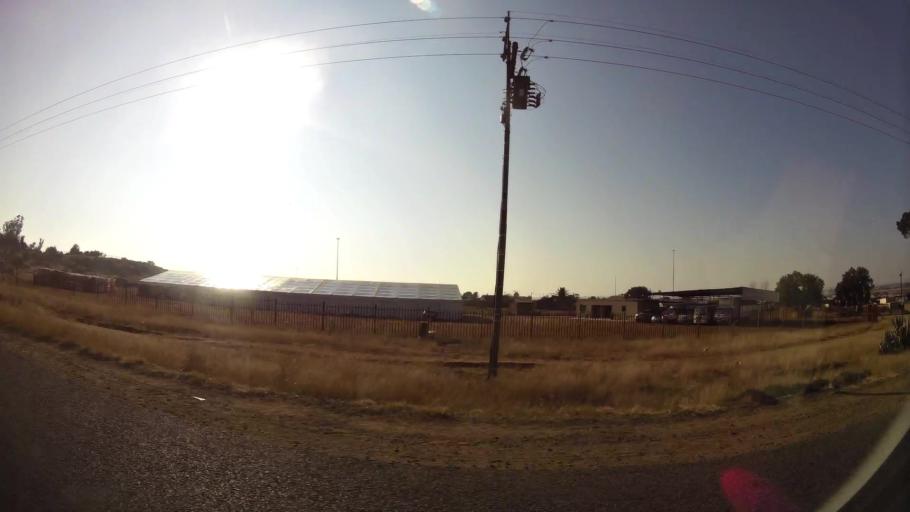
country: ZA
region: Orange Free State
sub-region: Mangaung Metropolitan Municipality
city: Bloemfontein
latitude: -29.1916
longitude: 26.2719
